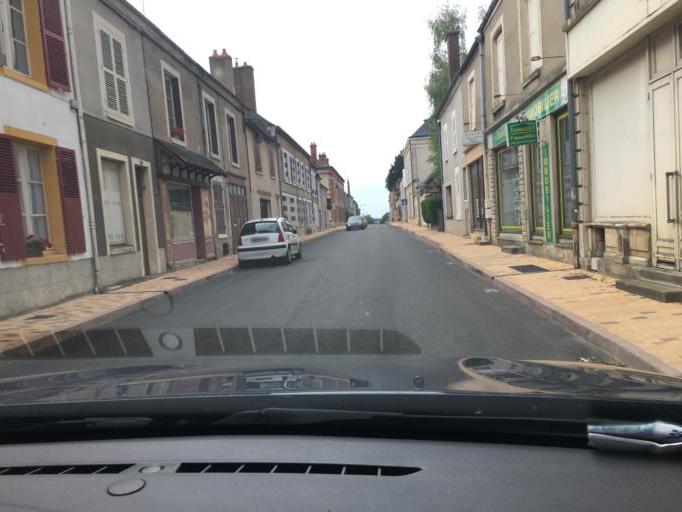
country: FR
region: Centre
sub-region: Departement du Cher
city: Henrichemont
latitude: 47.3032
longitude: 2.5240
